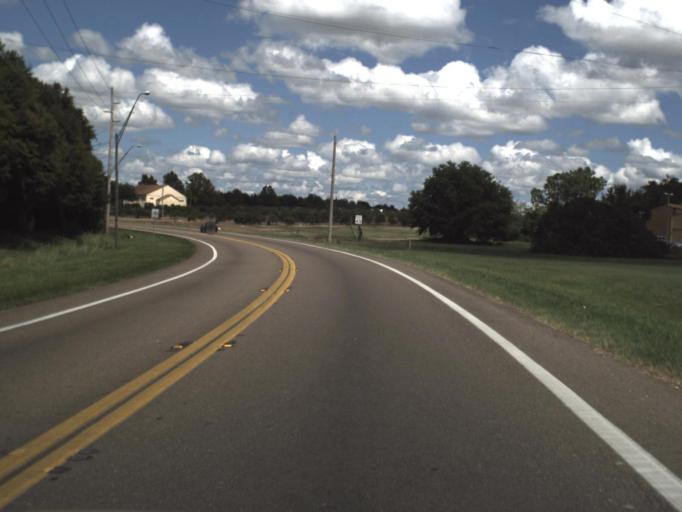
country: US
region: Florida
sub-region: Polk County
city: Winter Haven
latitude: 28.0499
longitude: -81.7220
